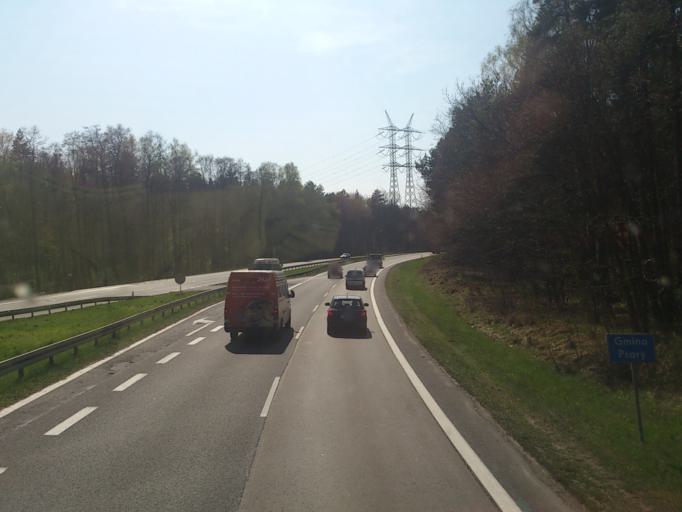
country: PL
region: Silesian Voivodeship
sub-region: Powiat bedzinski
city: Sarnow
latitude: 50.3859
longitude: 19.1813
